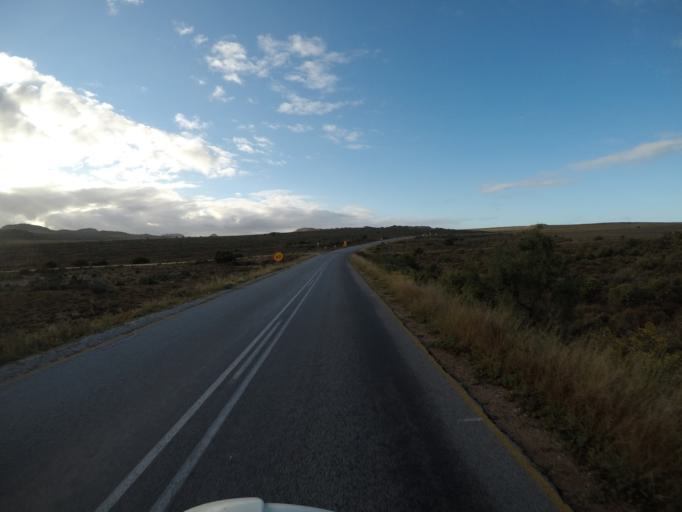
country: ZA
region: Western Cape
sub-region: West Coast District Municipality
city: Clanwilliam
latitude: -32.3317
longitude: 18.3719
